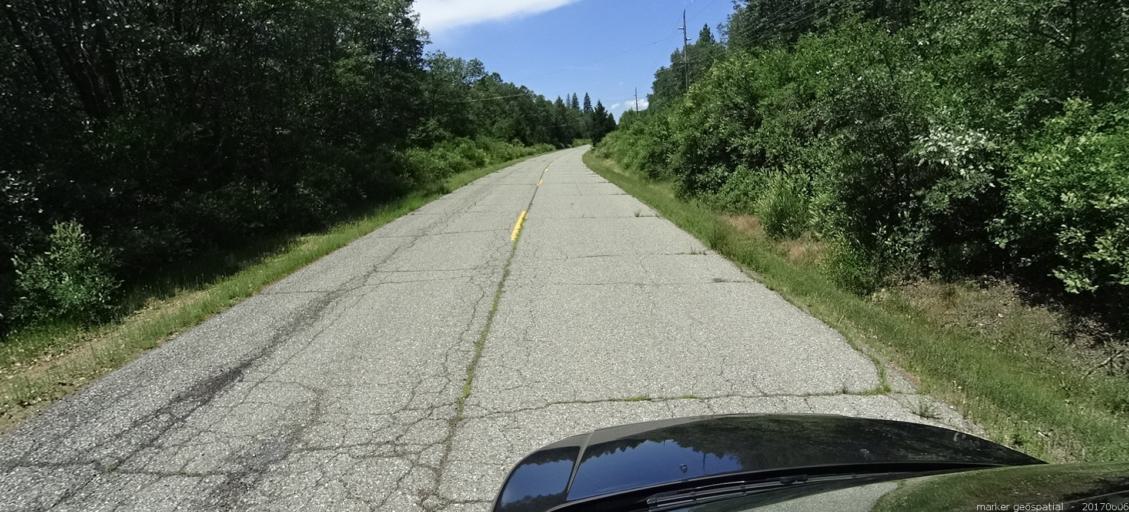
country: US
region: California
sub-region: Siskiyou County
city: Dunsmuir
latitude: 41.2534
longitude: -122.2616
